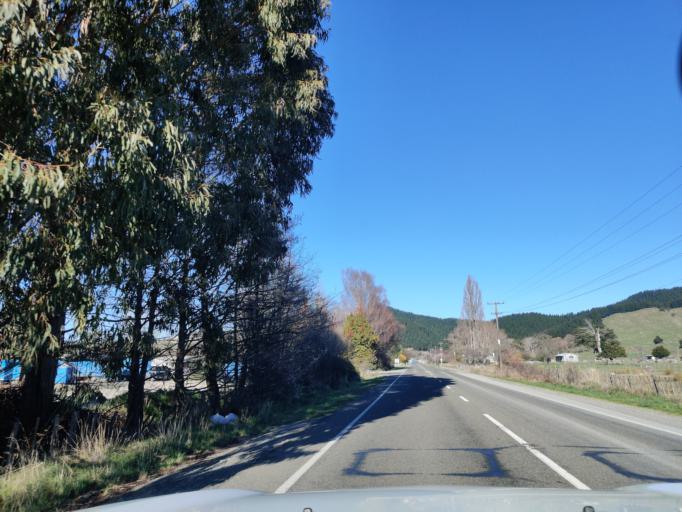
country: NZ
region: Manawatu-Wanganui
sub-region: Ruapehu District
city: Waiouru
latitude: -39.8137
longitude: 175.7838
